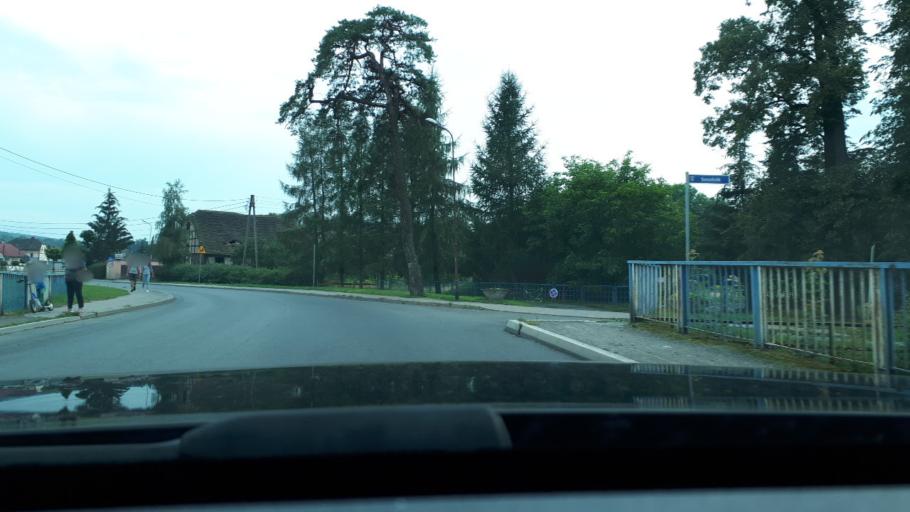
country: PL
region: Lower Silesian Voivodeship
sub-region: Powiat lubanski
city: Lesna
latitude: 51.0244
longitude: 15.2615
